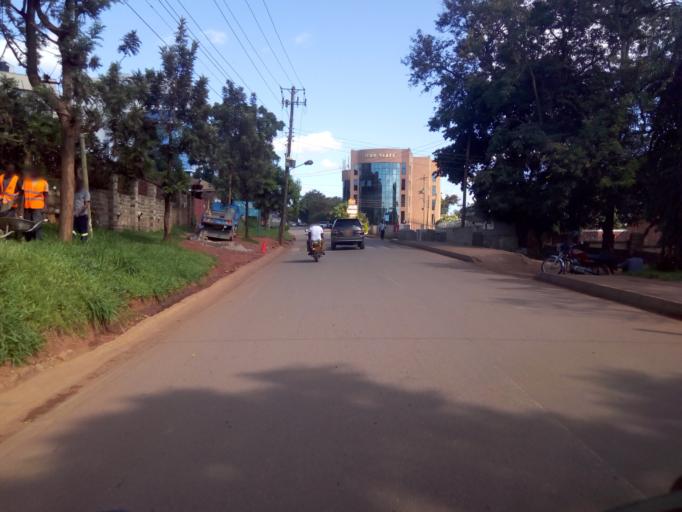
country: UG
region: Central Region
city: Kampala Central Division
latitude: 0.3227
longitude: 32.5763
